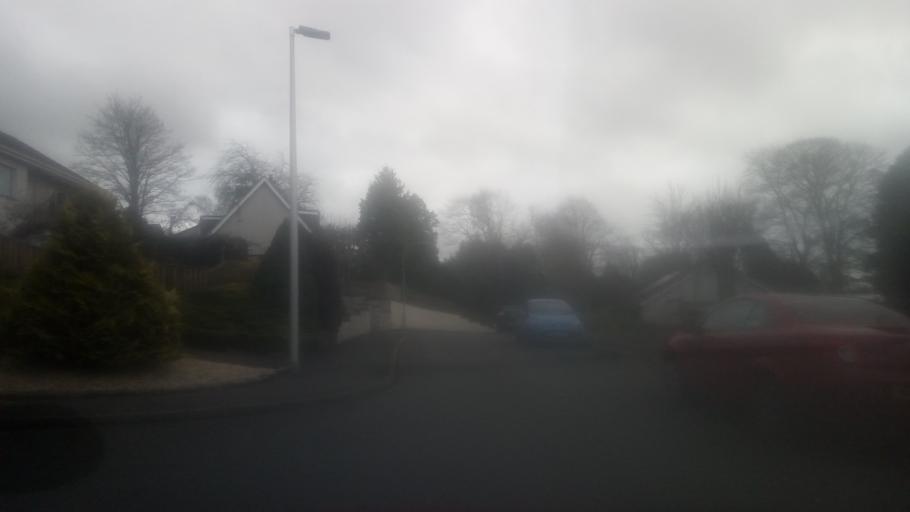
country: GB
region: Scotland
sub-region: The Scottish Borders
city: Jedburgh
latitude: 55.4752
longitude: -2.5510
